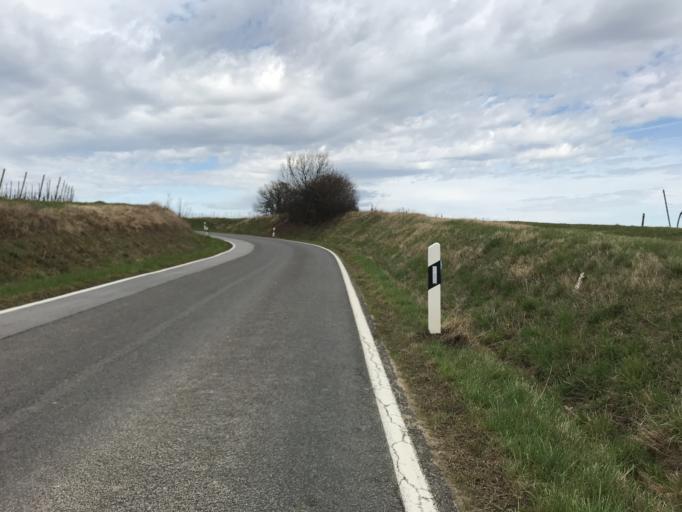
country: DE
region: Rheinland-Pfalz
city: Partenheim
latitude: 49.8807
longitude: 8.0928
